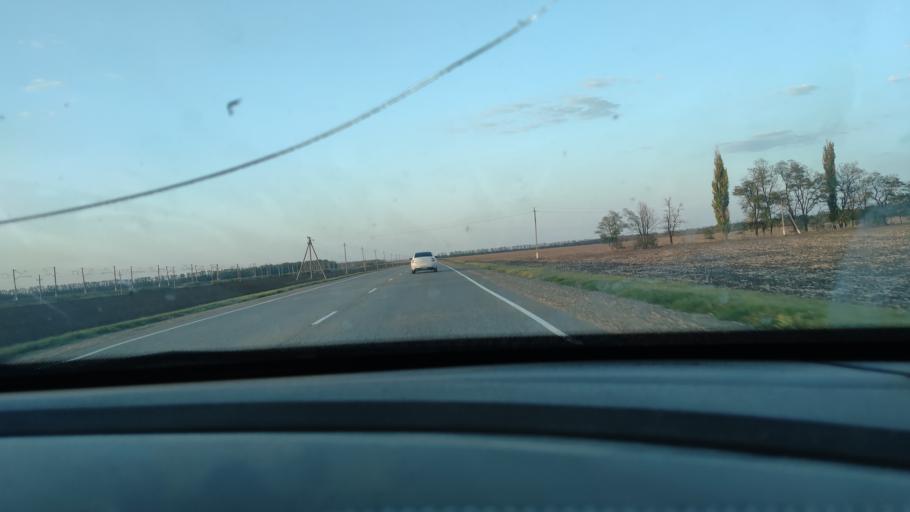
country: RU
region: Krasnodarskiy
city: Novominskaya
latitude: 46.3594
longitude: 38.9671
